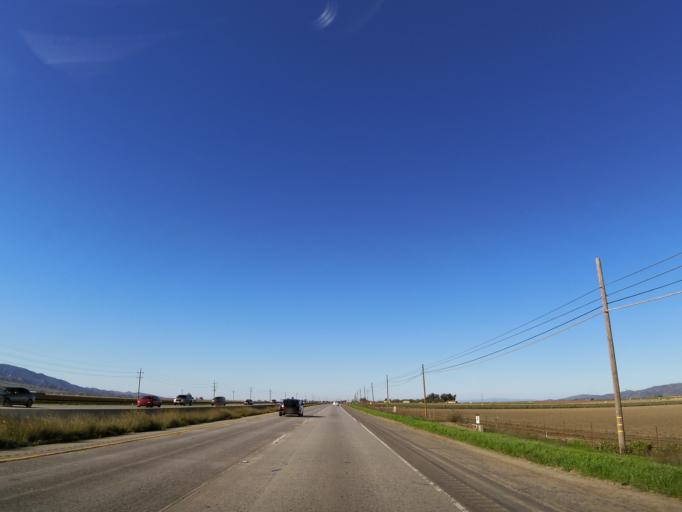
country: US
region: California
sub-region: Monterey County
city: Chualar
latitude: 36.5512
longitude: -121.4988
